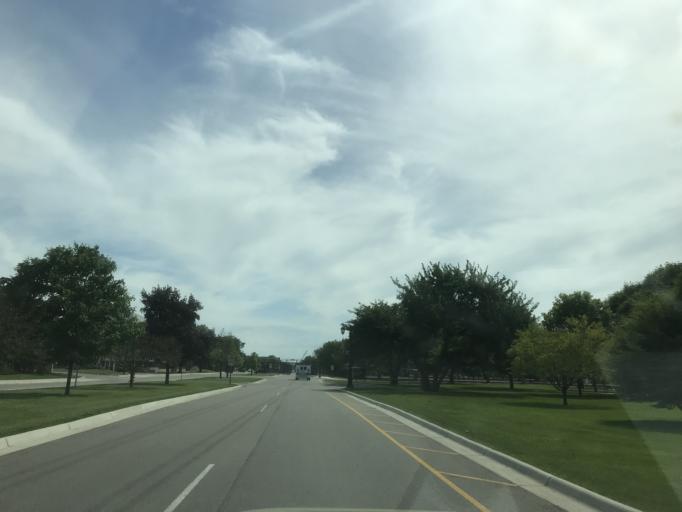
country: US
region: Michigan
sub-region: Wayne County
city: Allen Park
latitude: 42.3024
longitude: -83.2322
